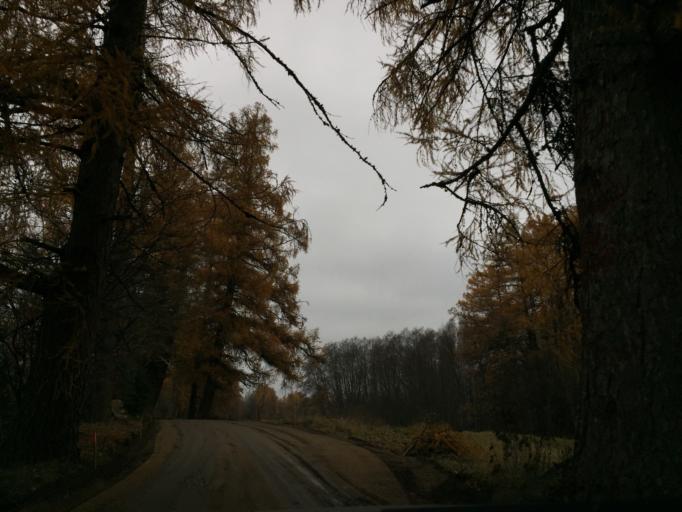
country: LV
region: Pargaujas
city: Stalbe
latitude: 57.5091
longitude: 25.0005
